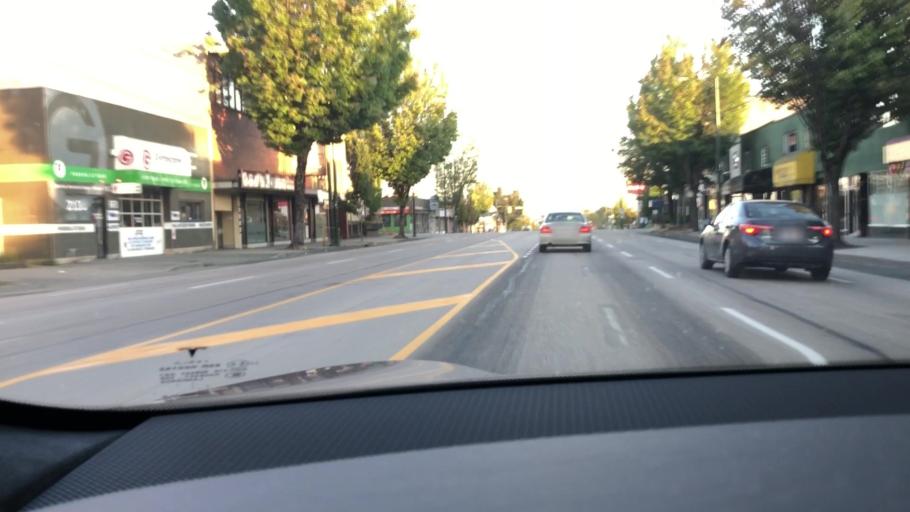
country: CA
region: British Columbia
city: Vancouver
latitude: 49.2441
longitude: -123.0627
